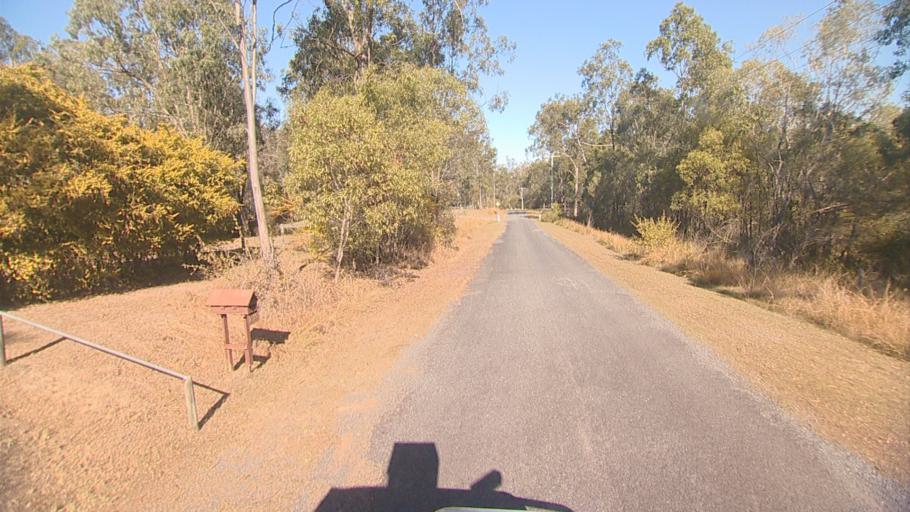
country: AU
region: Queensland
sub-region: Logan
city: Cedar Vale
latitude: -27.8462
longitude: 153.0584
